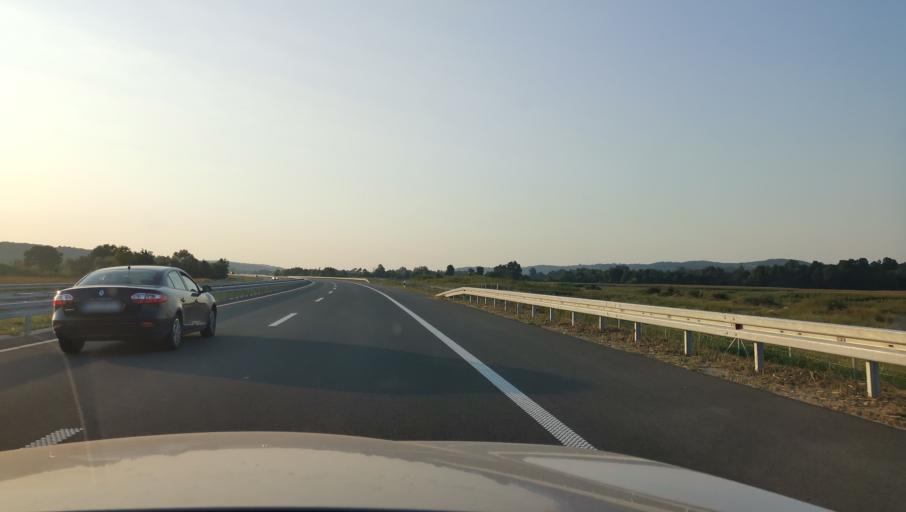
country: RS
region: Central Serbia
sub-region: Kolubarski Okrug
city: Ljig
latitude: 44.3045
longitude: 20.2303
